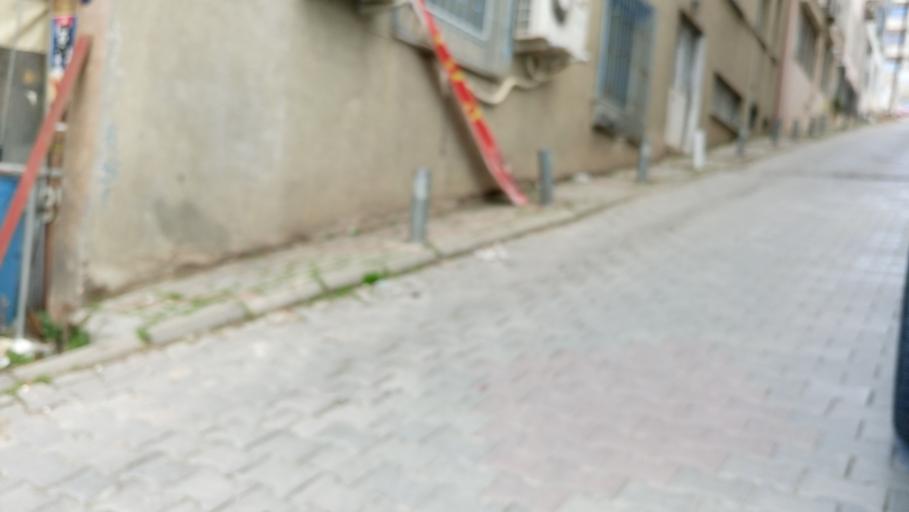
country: TR
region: Izmir
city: Izmir
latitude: 38.4068
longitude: 27.1063
